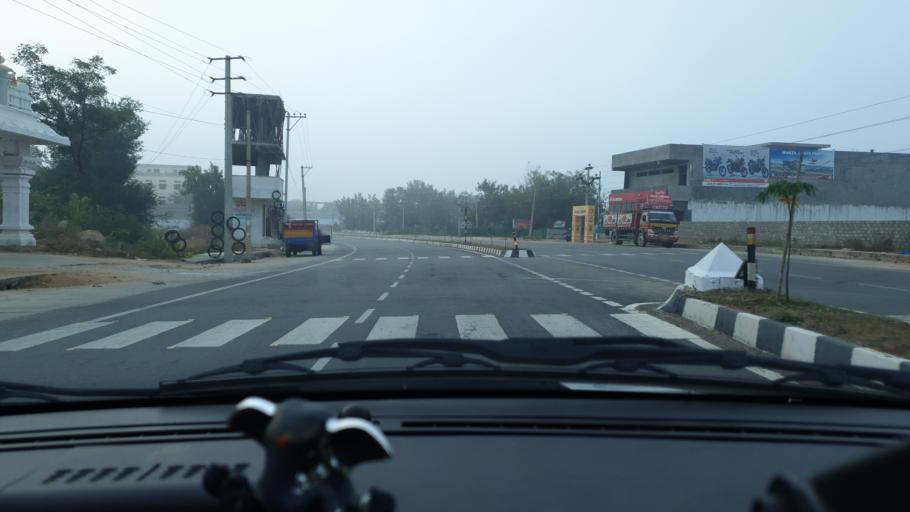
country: IN
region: Telangana
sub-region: Mahbubnagar
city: Farrukhnagar
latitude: 16.8612
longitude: 78.5283
